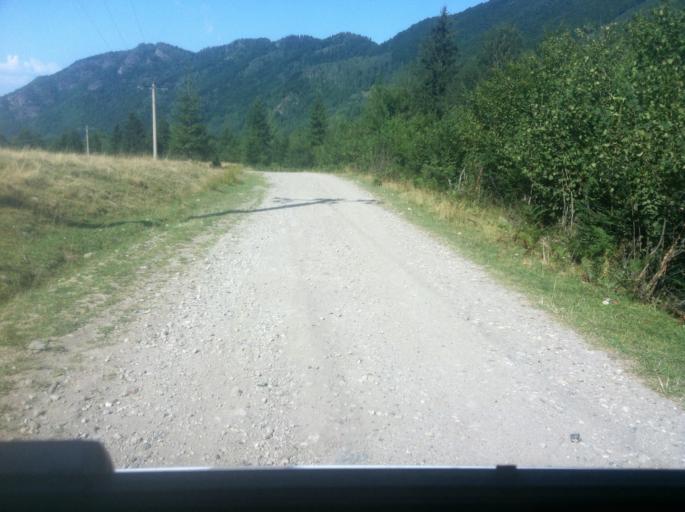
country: RO
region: Hunedoara
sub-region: Comuna Rau de Mori
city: Rau de Mori
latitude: 45.4417
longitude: 22.8932
